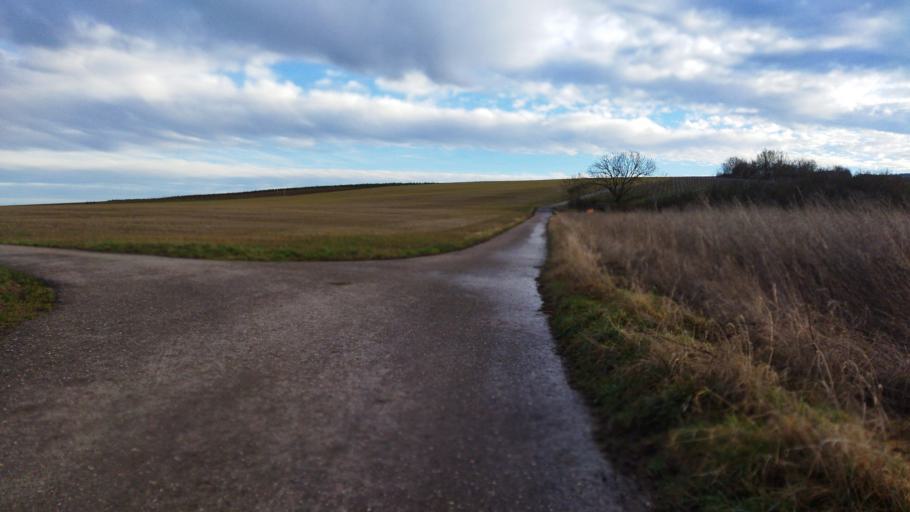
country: DE
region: Baden-Wuerttemberg
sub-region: Regierungsbezirk Stuttgart
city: Cleebronn
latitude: 49.0603
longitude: 9.0374
